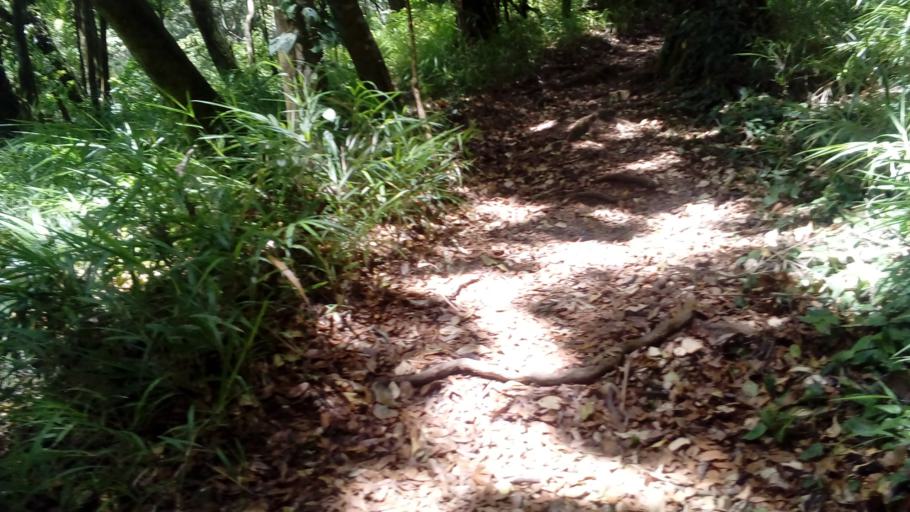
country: CR
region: Alajuela
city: Sabanilla
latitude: 10.1573
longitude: -84.2400
